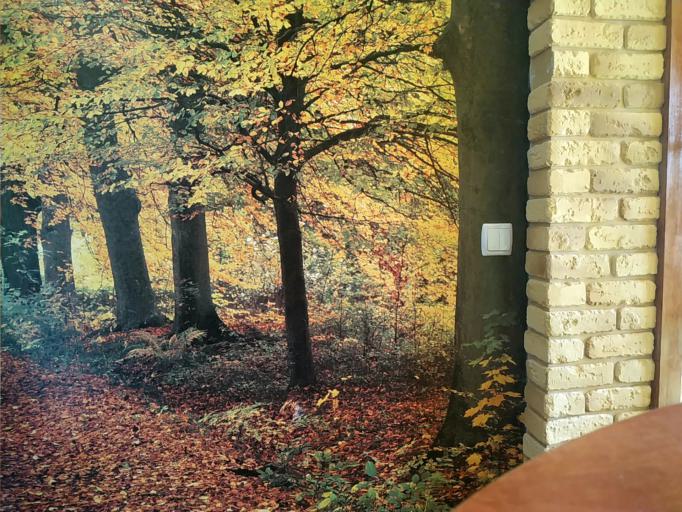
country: RU
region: Jaroslavl
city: Kukoboy
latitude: 58.9106
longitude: 39.6848
